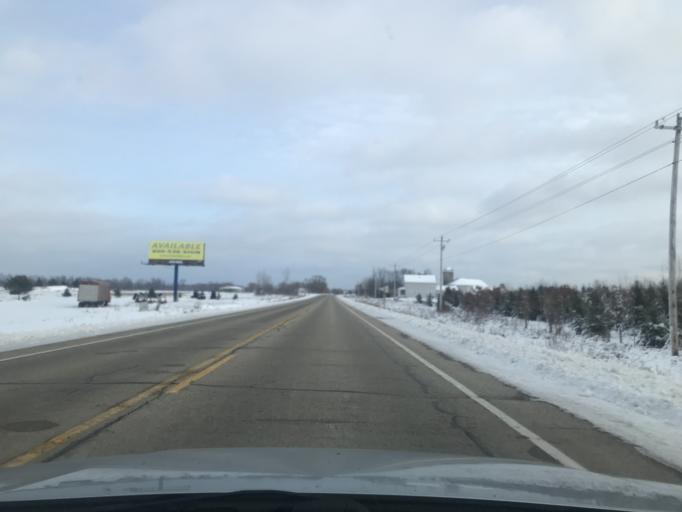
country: US
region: Wisconsin
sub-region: Oconto County
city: Oconto
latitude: 44.8927
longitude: -87.9426
